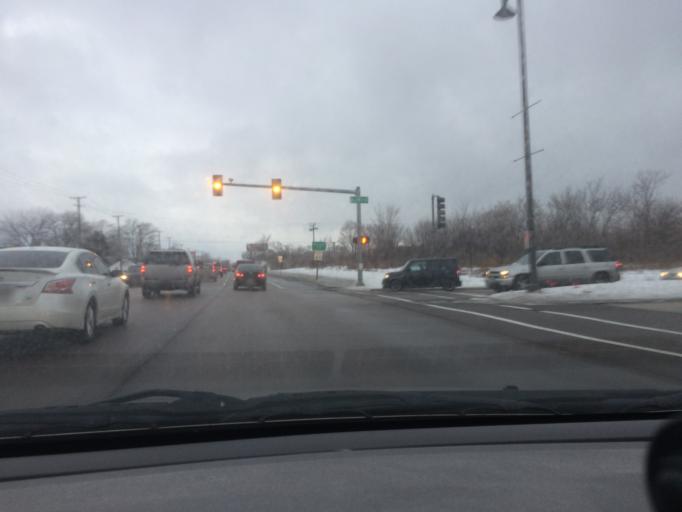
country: US
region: Illinois
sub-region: Cook County
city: Bartlett
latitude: 42.0016
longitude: -88.1751
